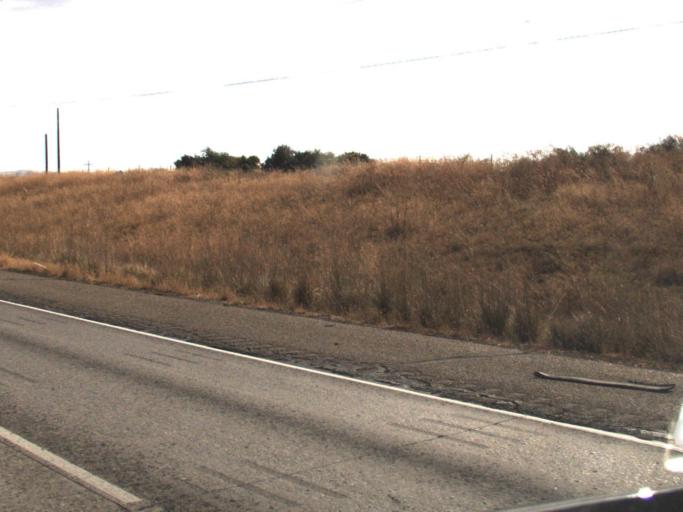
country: US
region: Washington
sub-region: Yakima County
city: Grandview
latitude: 46.2803
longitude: -119.9376
